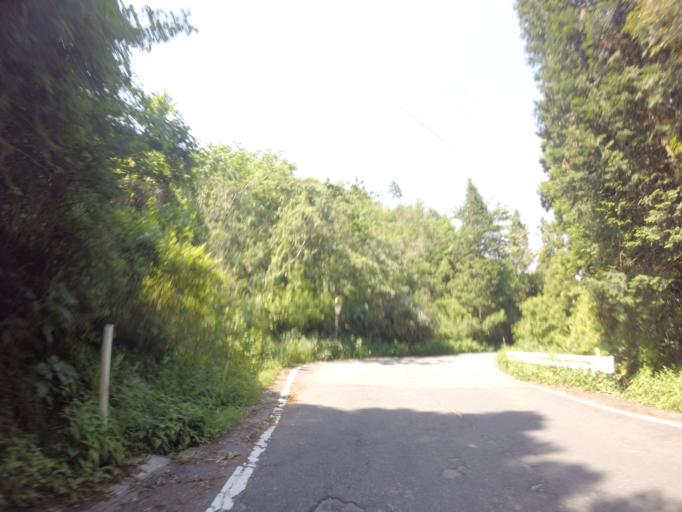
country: JP
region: Shizuoka
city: Fujinomiya
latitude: 35.1577
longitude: 138.5693
